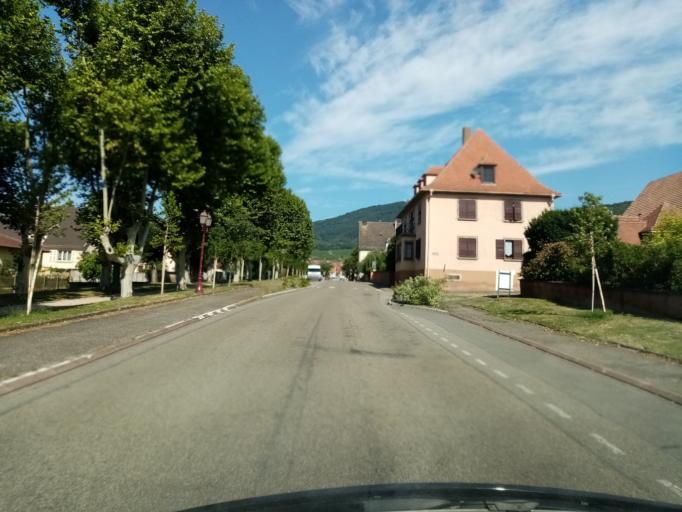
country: FR
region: Alsace
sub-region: Departement du Haut-Rhin
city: Saint-Hippolyte
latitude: 48.2298
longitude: 7.3748
